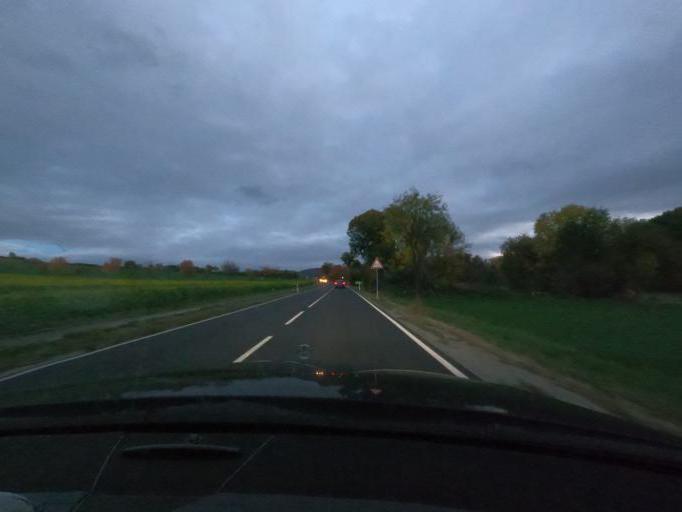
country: DE
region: Thuringia
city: Arenshausen
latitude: 51.3921
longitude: 9.9493
